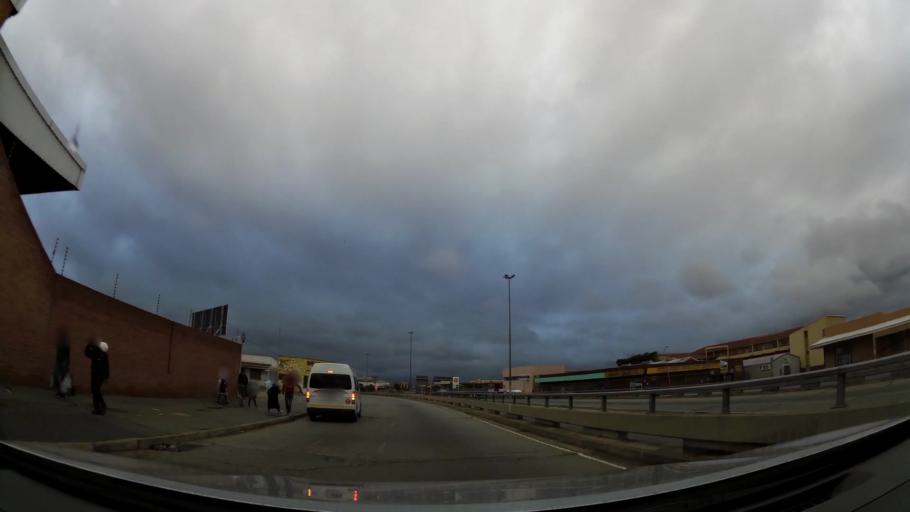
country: ZA
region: Eastern Cape
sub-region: Nelson Mandela Bay Metropolitan Municipality
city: Port Elizabeth
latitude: -33.9218
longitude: 25.5928
